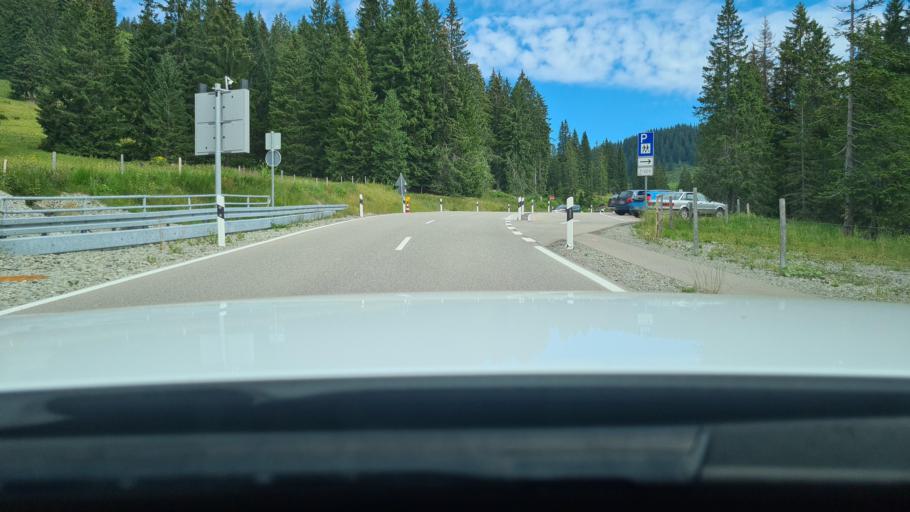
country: DE
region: Bavaria
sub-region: Swabia
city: Obermaiselstein
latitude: 47.4354
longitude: 10.1732
